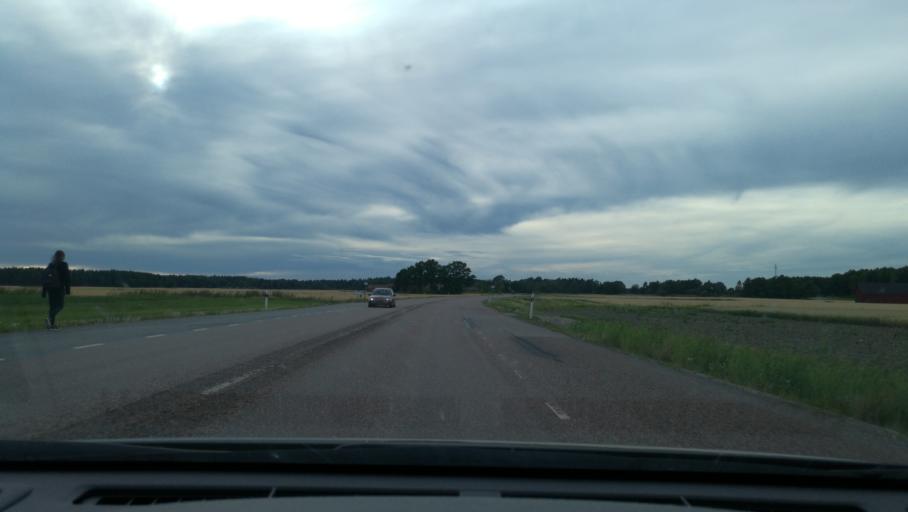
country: SE
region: Vaestmanland
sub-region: Kopings Kommun
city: Koping
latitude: 59.4595
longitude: 16.0060
